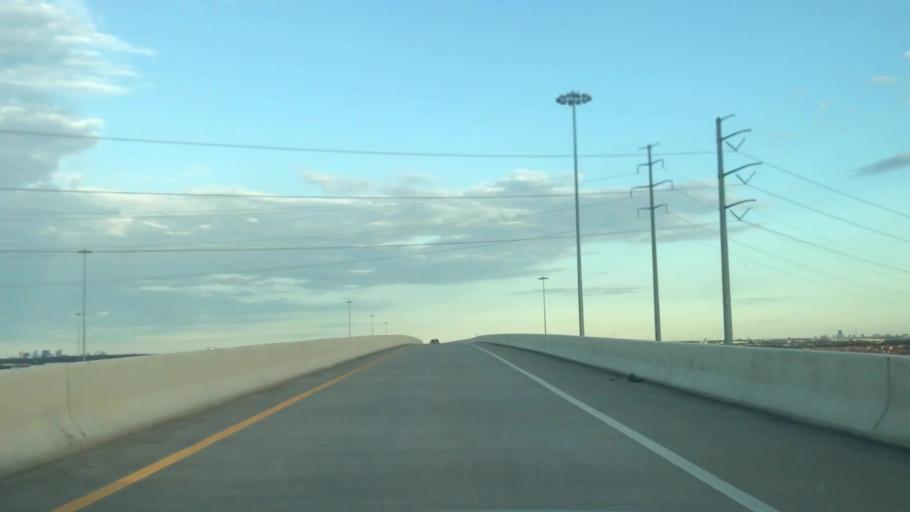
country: US
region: Texas
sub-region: Dallas County
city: Farmers Branch
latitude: 32.9120
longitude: -96.9464
